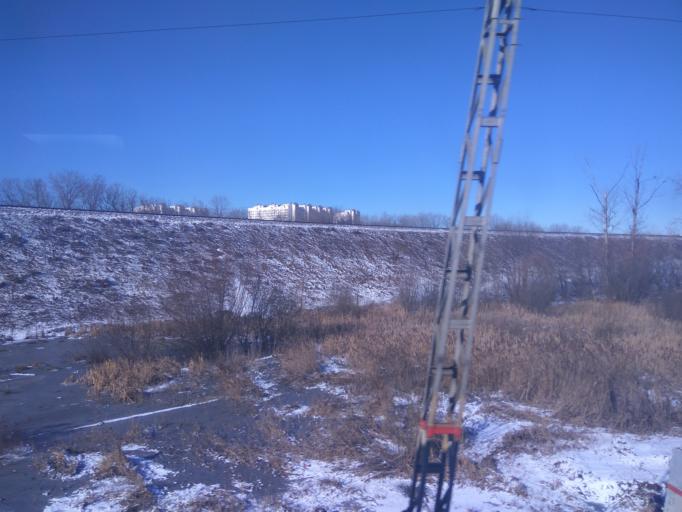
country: RU
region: Moscow
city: Tekstil'shchiki
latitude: 55.6954
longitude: 37.7311
